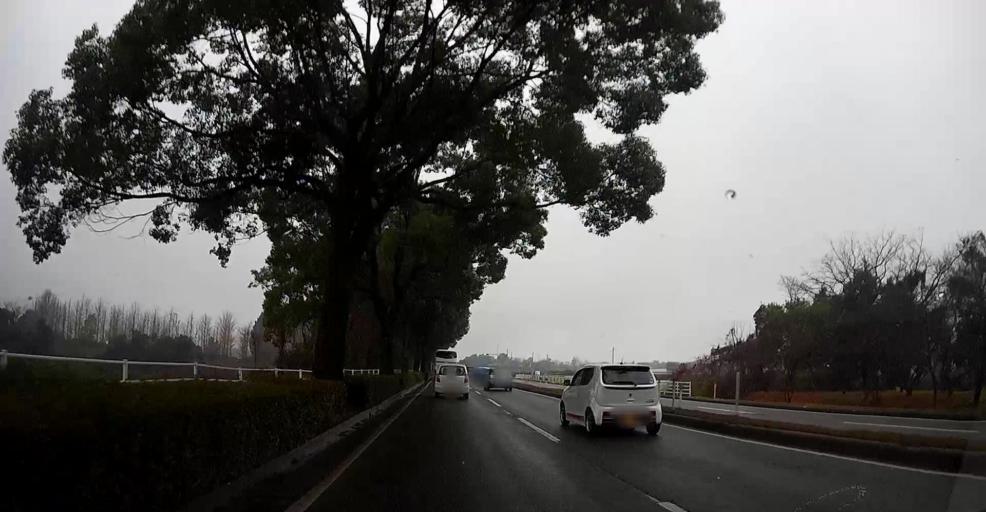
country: JP
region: Kumamoto
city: Ozu
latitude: 32.8229
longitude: 130.8535
